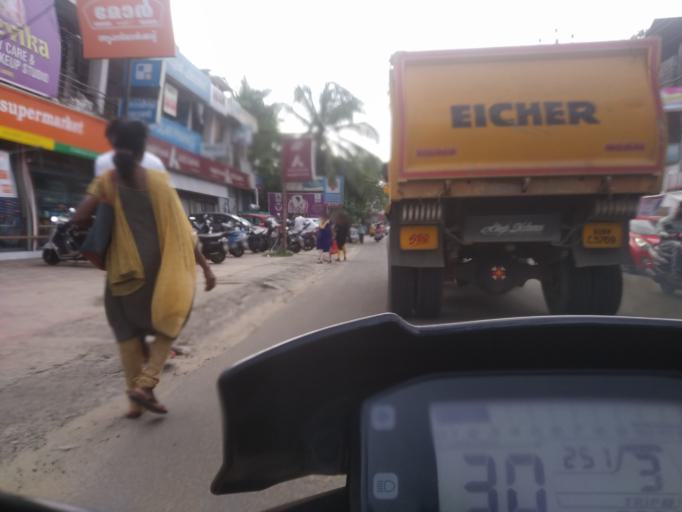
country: IN
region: Kerala
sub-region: Thrissur District
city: Kodungallur
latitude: 10.1437
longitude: 76.2279
